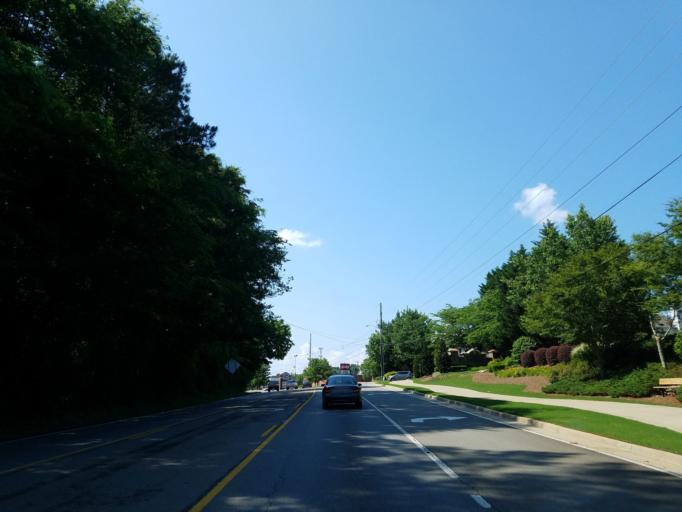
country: US
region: Georgia
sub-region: Cherokee County
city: Holly Springs
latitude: 34.1384
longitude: -84.5031
